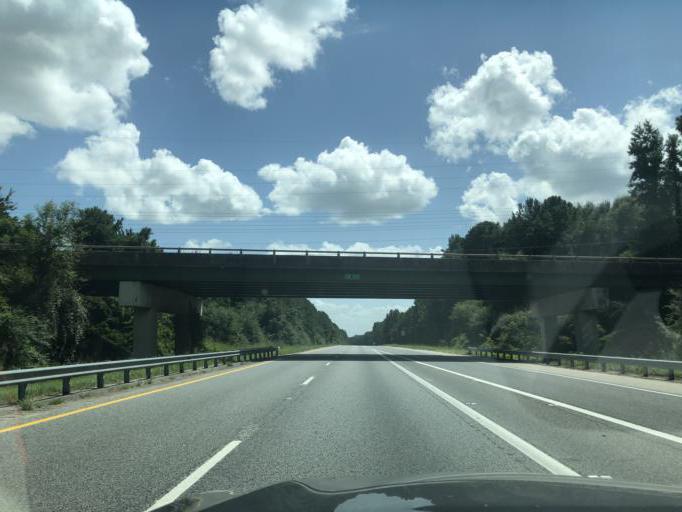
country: US
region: Georgia
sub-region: Troup County
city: La Grange
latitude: 33.0429
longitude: -84.9509
